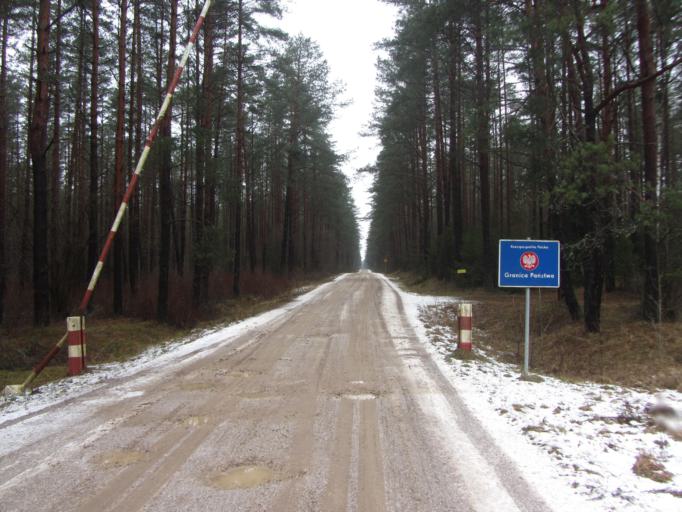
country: LT
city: Veisiejai
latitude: 54.0456
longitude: 23.5263
